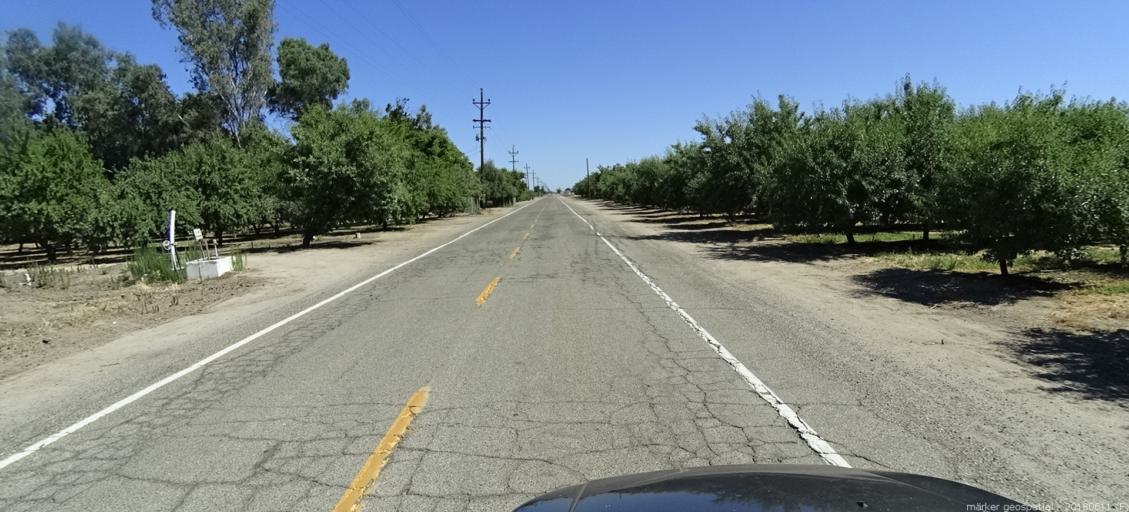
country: US
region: California
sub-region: Madera County
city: Fairmead
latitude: 36.9434
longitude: -120.2018
